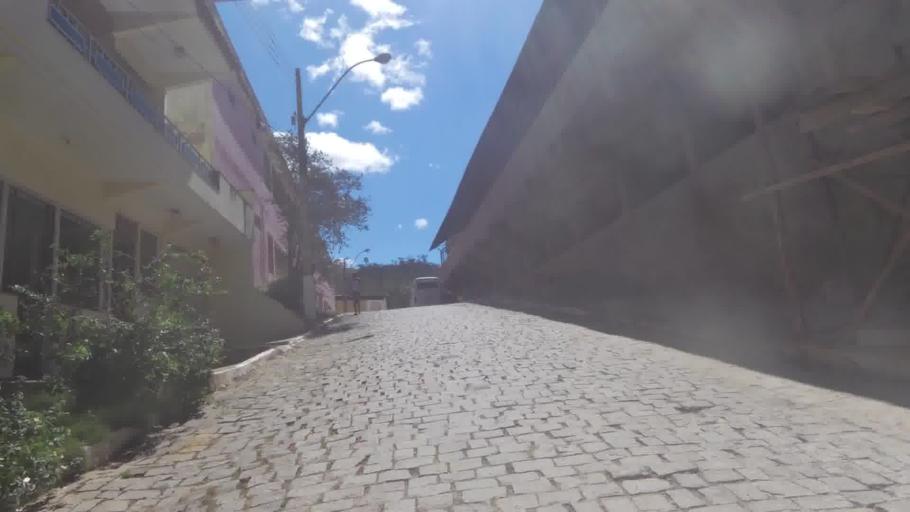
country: BR
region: Espirito Santo
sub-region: Cachoeiro De Itapemirim
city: Cachoeiro de Itapemirim
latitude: -20.9133
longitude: -41.1966
